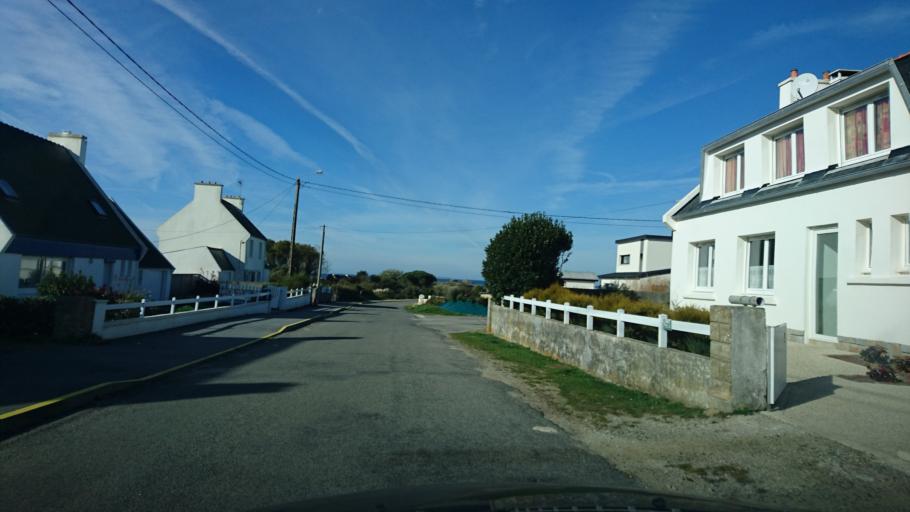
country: FR
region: Brittany
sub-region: Departement du Finistere
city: Lampaul-Plouarzel
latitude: 48.4366
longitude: -4.7765
